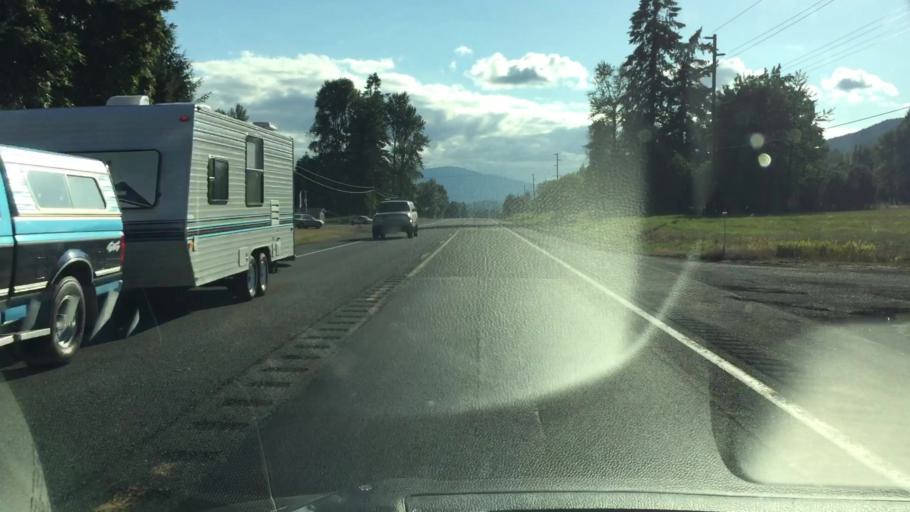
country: US
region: Washington
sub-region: Lewis County
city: Morton
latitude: 46.5345
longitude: -122.1210
